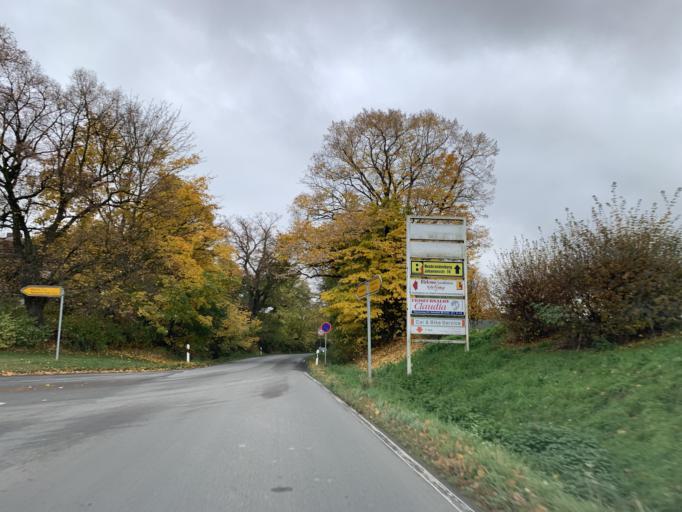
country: DE
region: Mecklenburg-Vorpommern
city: Neverin
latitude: 53.5870
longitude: 13.3307
